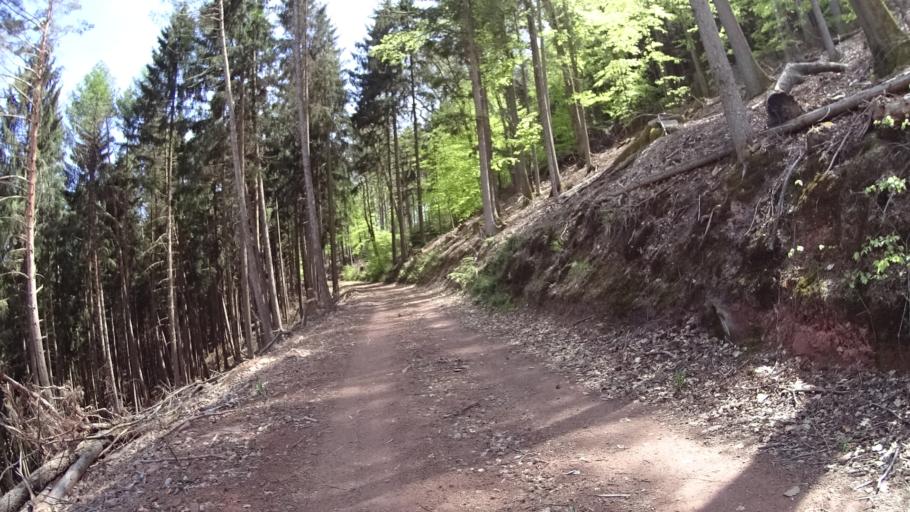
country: DE
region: Rheinland-Pfalz
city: Ramberg
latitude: 49.2987
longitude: 8.0068
